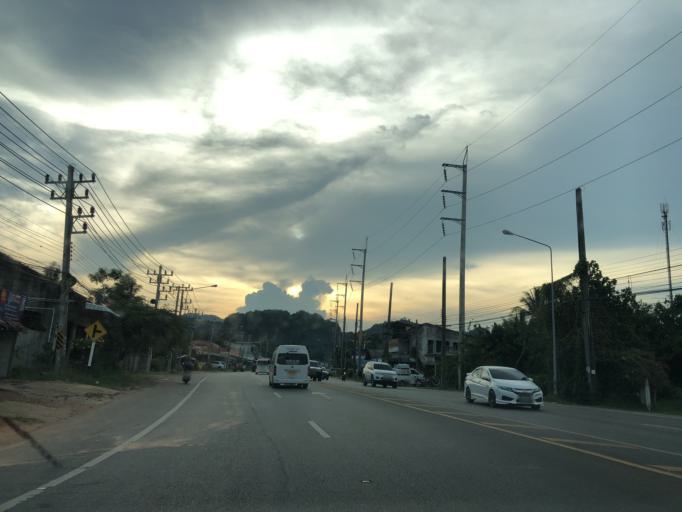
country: TH
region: Krabi
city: Krabi
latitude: 8.0847
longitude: 98.8869
